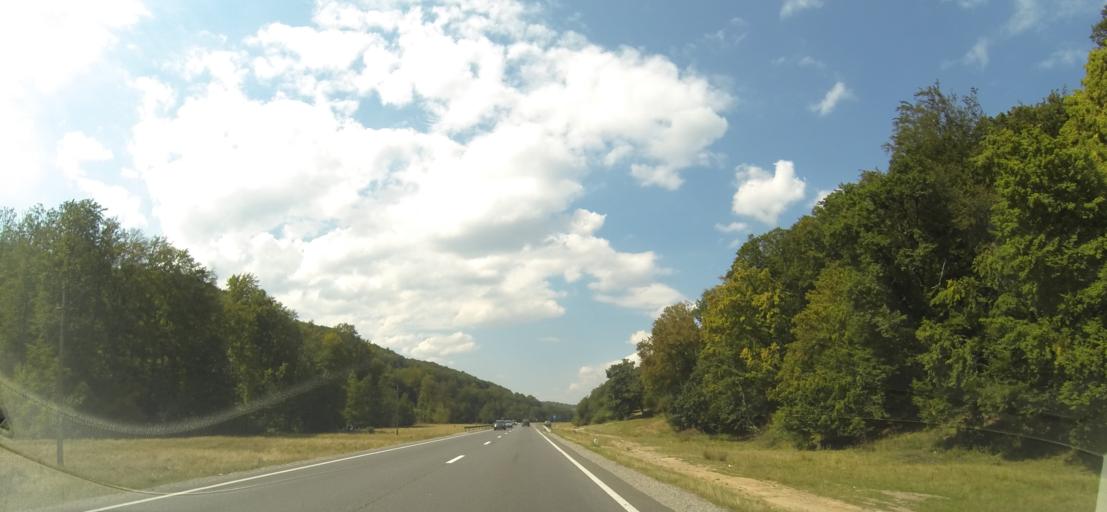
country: RO
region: Brasov
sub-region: Comuna Sinca Veche
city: Persani
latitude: 45.7579
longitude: 25.2419
